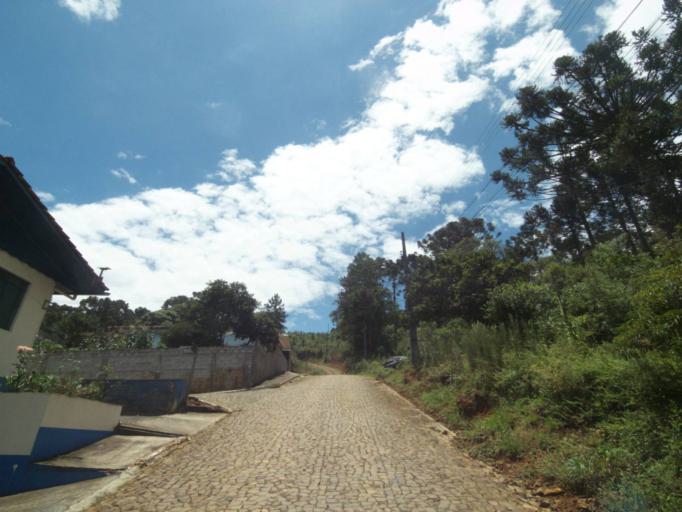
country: BR
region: Parana
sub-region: Pinhao
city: Pinhao
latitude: -26.1551
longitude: -51.5566
